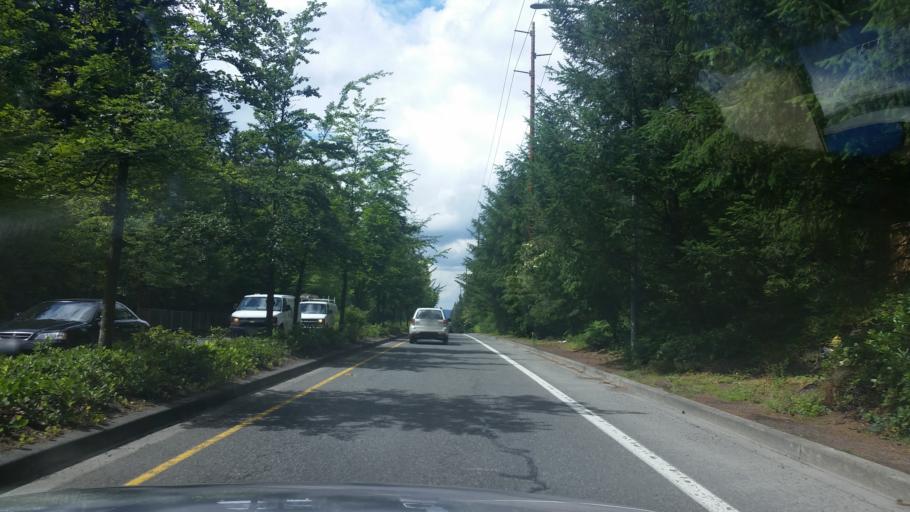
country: US
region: Washington
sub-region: King County
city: Union Hill-Novelty Hill
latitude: 47.6966
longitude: -122.0386
